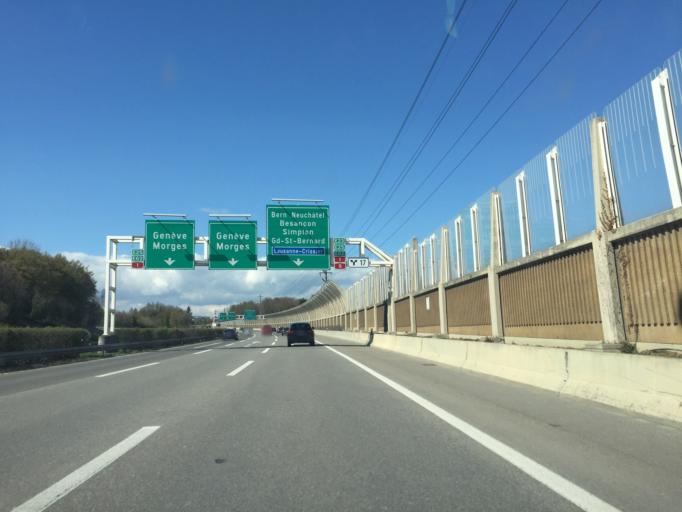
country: CH
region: Vaud
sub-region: Ouest Lausannois District
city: Chavannes
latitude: 46.5362
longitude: 6.5708
